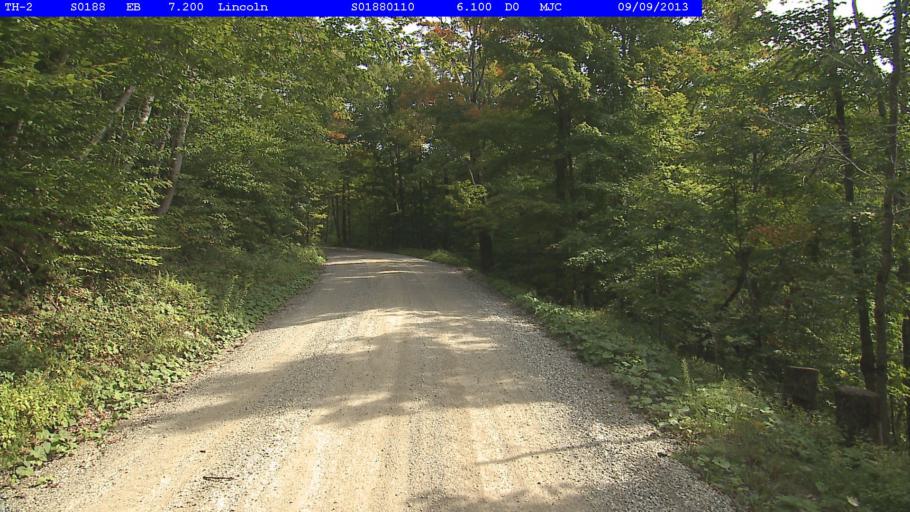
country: US
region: Vermont
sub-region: Addison County
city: Bristol
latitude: 44.0907
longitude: -72.9372
